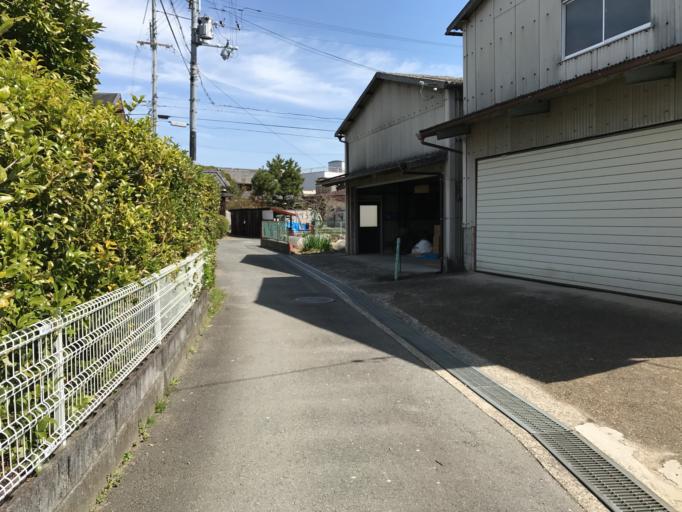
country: JP
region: Kyoto
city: Tanabe
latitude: 34.7804
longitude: 135.7971
